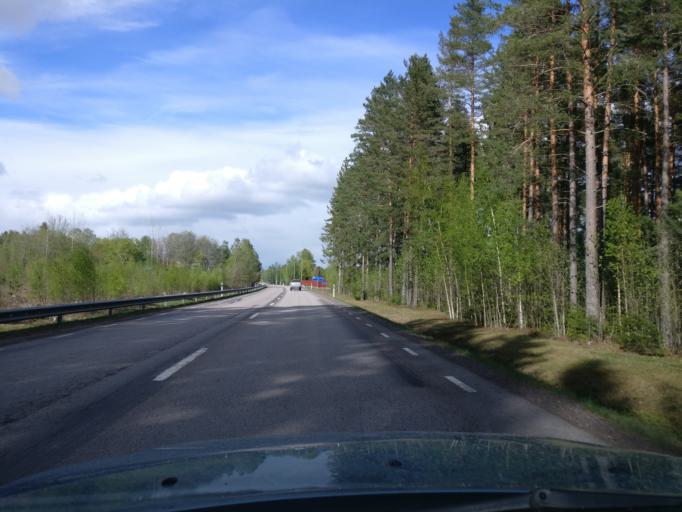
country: SE
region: Vaermland
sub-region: Forshaga Kommun
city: Forshaga
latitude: 59.4900
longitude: 13.4230
